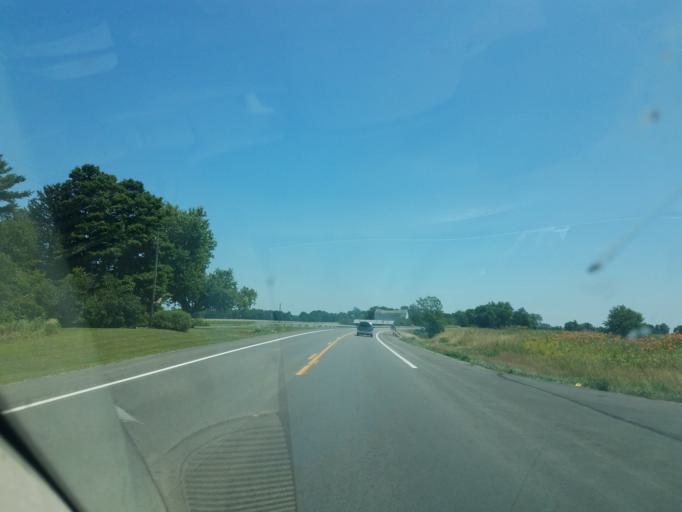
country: US
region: Ohio
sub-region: Hardin County
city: Ada
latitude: 40.7180
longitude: -83.7675
